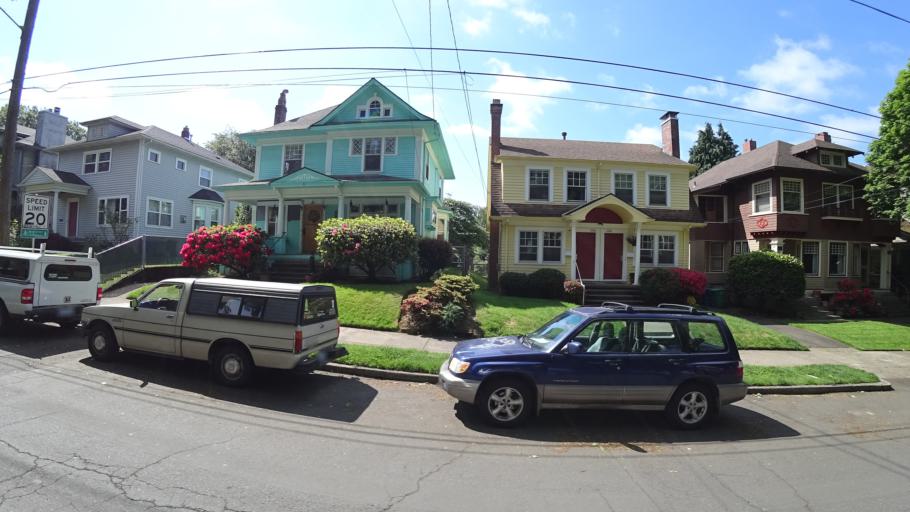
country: US
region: Oregon
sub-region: Multnomah County
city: Portland
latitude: 45.5143
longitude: -122.6415
